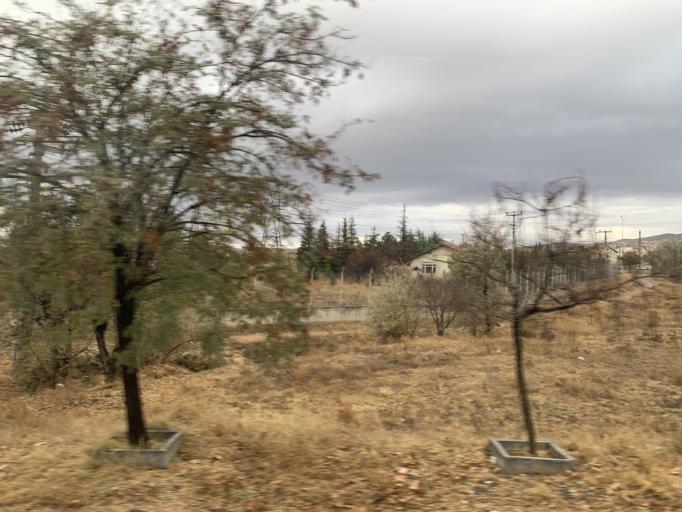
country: TR
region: Nevsehir
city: Avanos
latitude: 38.7205
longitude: 34.8616
